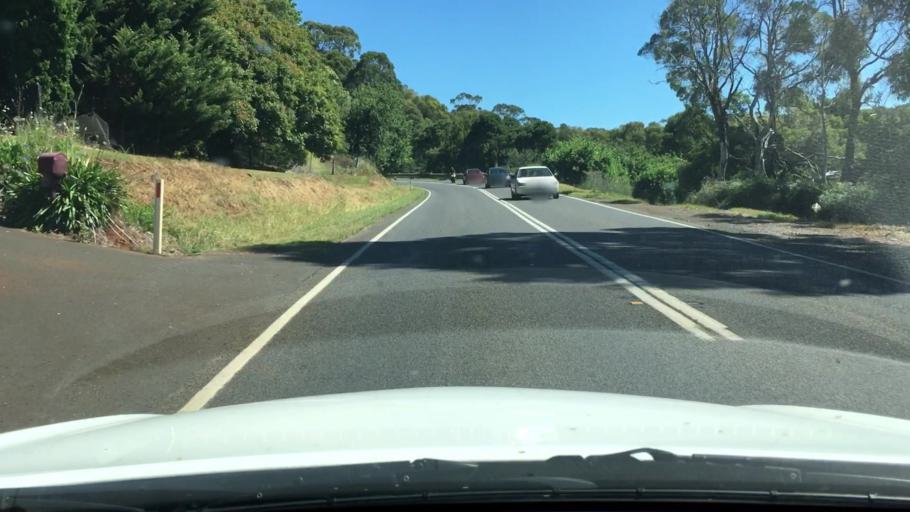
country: AU
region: Victoria
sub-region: Yarra Ranges
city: Mount Evelyn
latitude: -37.8154
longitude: 145.4067
